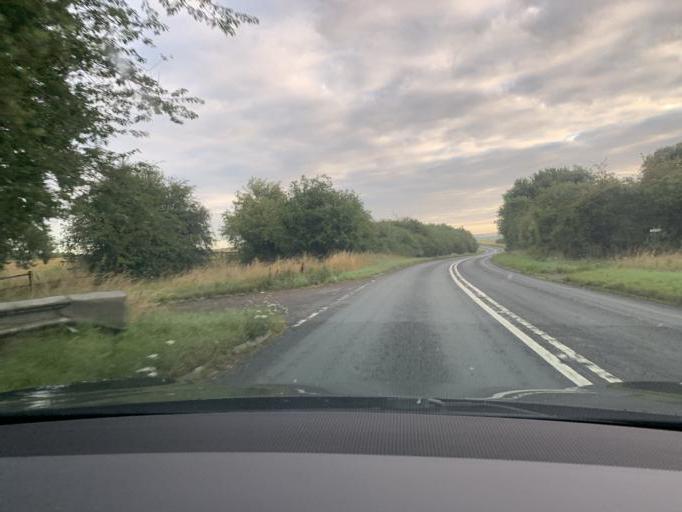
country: GB
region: England
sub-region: Wiltshire
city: Tidworth
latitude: 51.2575
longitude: -1.6674
